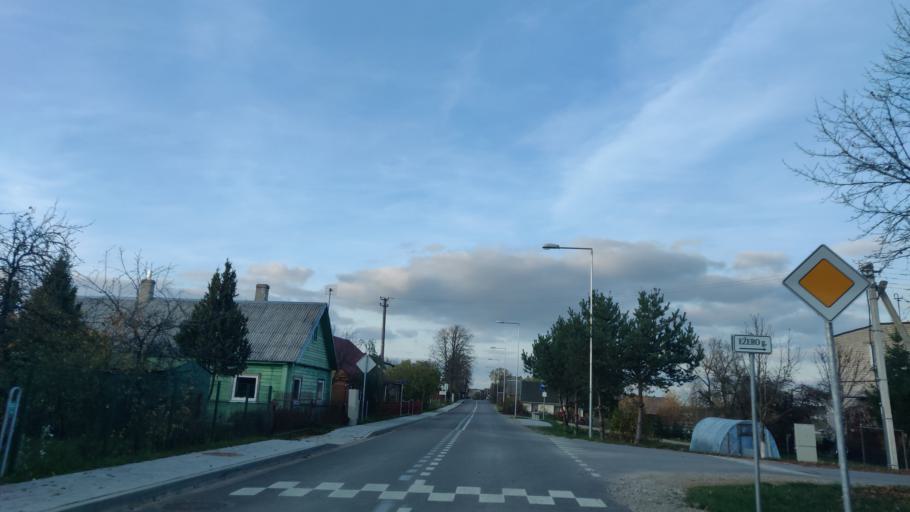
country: LT
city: Lentvaris
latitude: 54.5835
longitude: 25.0514
